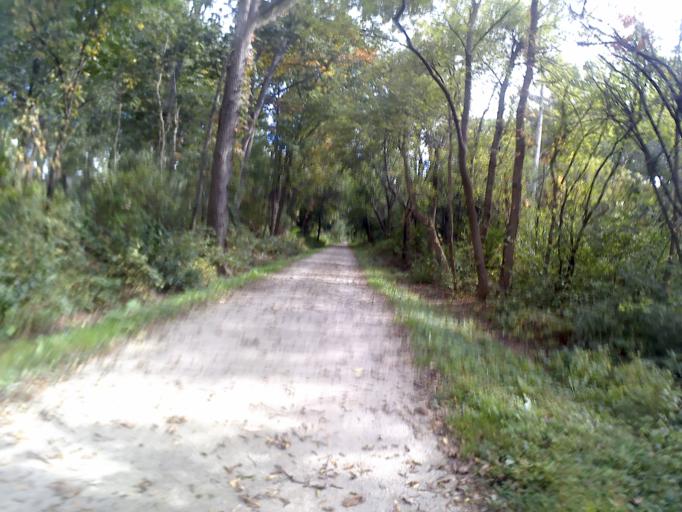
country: US
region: Illinois
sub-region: DuPage County
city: Wayne
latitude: 41.9261
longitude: -88.2143
